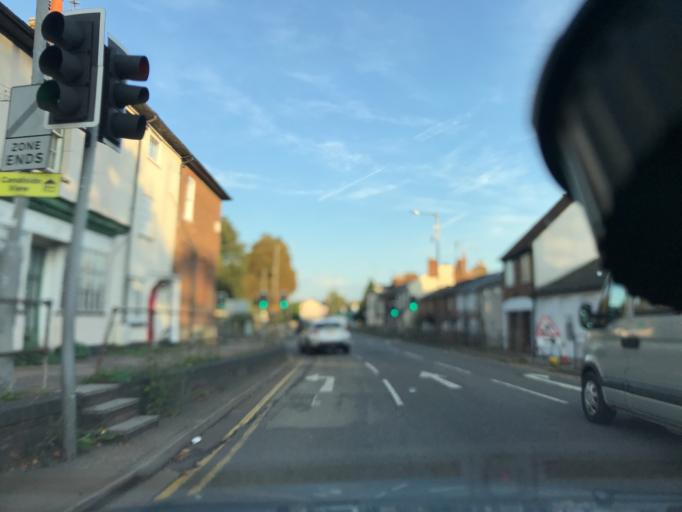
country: GB
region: England
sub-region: Buckinghamshire
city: Aylesbury
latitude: 51.8114
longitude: -0.8067
